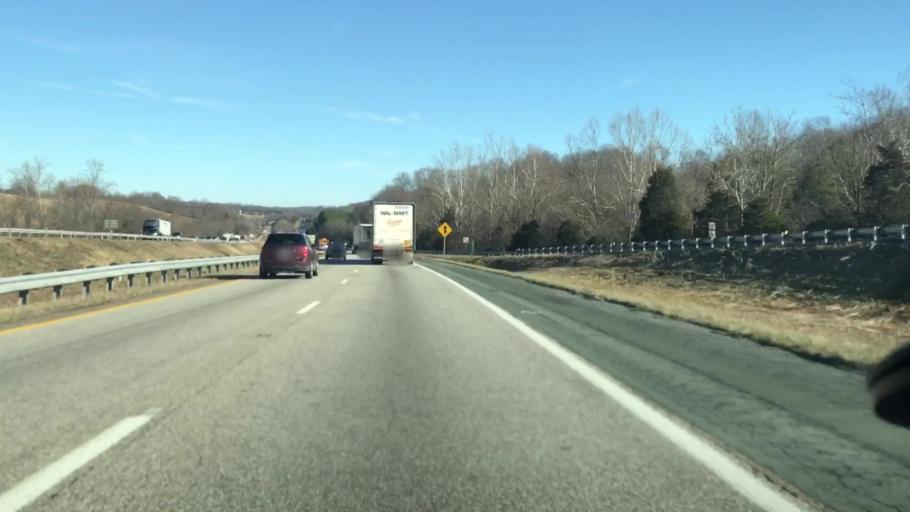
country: US
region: Virginia
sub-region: Rockbridge County
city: Glasgow
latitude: 37.6302
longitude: -79.5709
